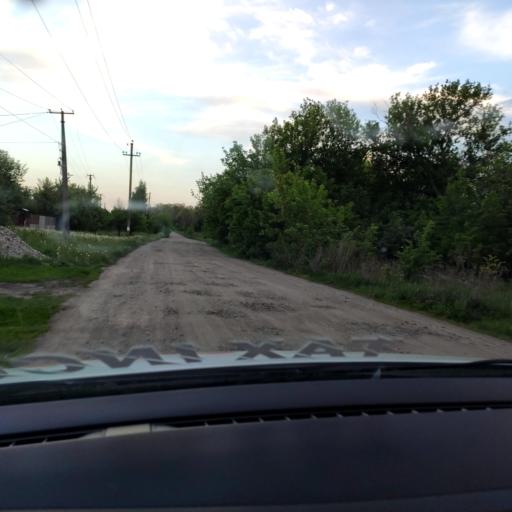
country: RU
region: Voronezj
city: Kolodeznyy
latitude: 51.4374
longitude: 39.2318
